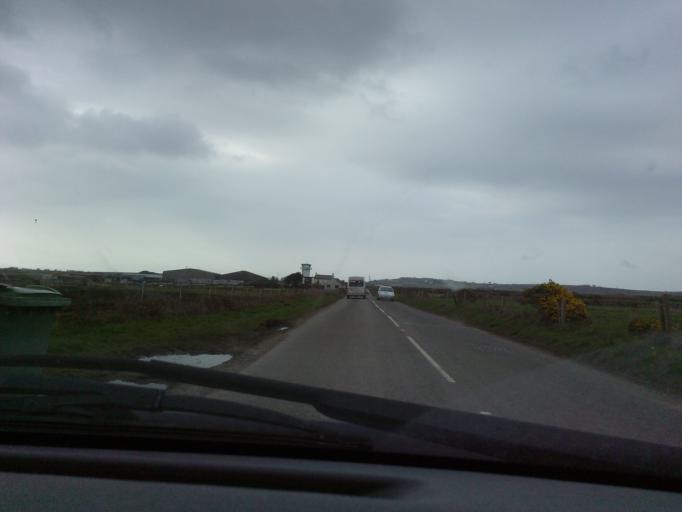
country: GB
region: England
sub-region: Cornwall
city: Saint Just
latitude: 50.0994
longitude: -5.6647
